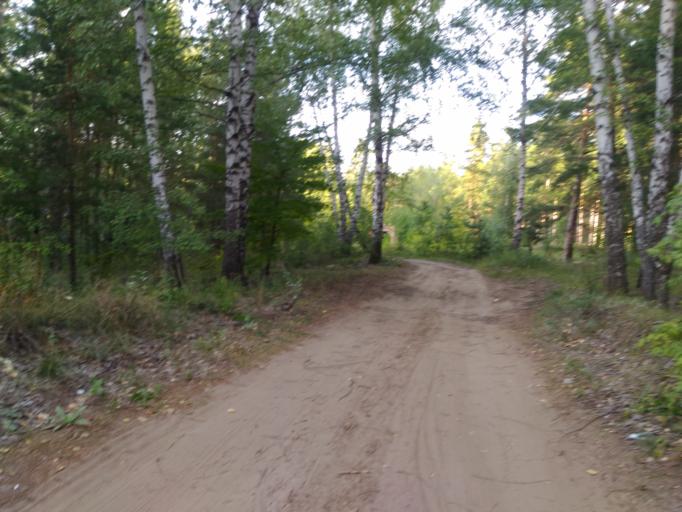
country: RU
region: Ulyanovsk
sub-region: Ulyanovskiy Rayon
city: Ulyanovsk
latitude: 54.3562
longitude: 48.5172
